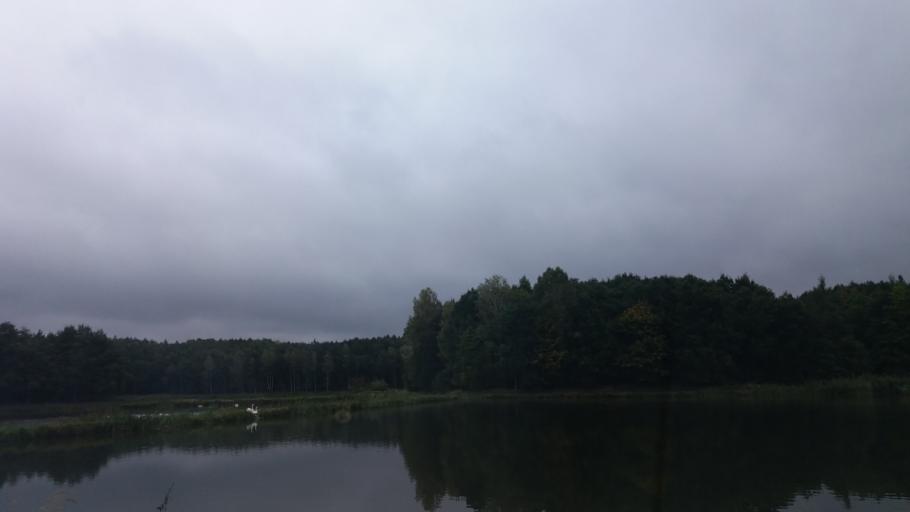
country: PL
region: West Pomeranian Voivodeship
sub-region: Powiat choszczenski
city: Pelczyce
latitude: 53.0683
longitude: 15.2828
